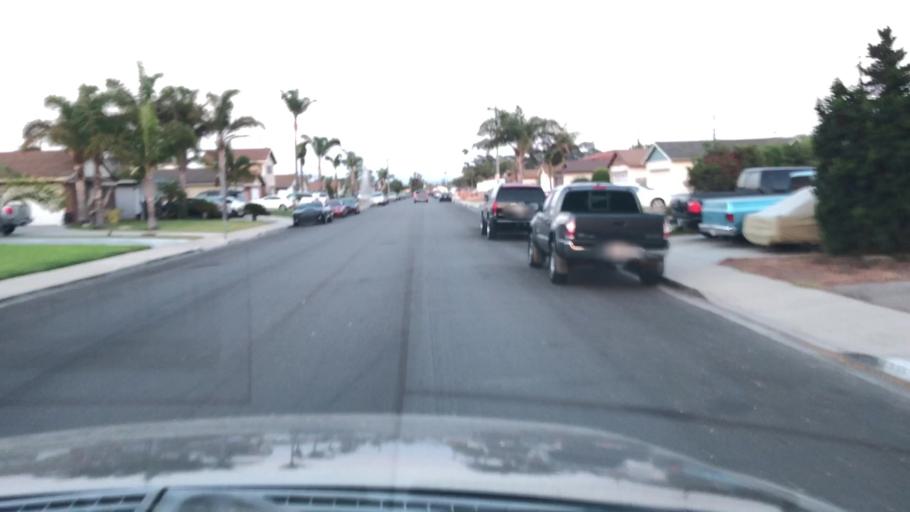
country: US
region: California
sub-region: Ventura County
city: Port Hueneme
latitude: 34.1656
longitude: -119.1920
